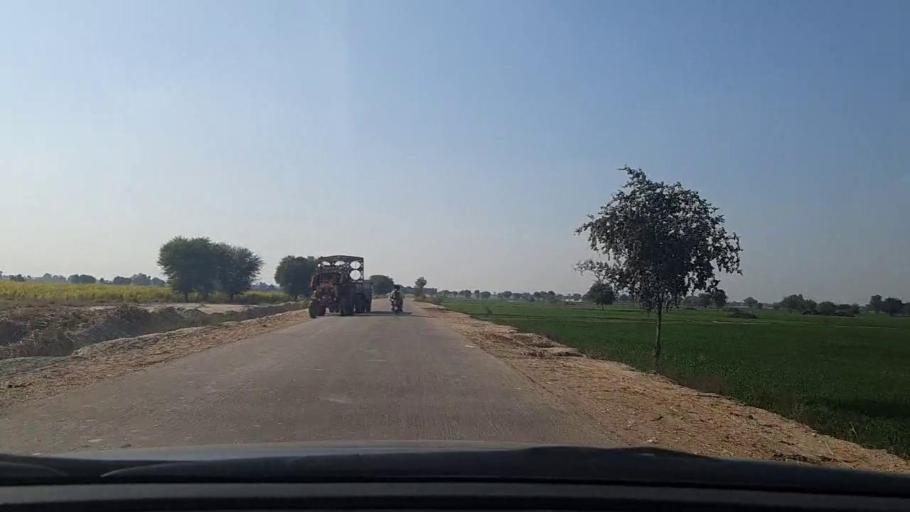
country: PK
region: Sindh
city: Daulatpur
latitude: 26.3183
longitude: 68.0547
